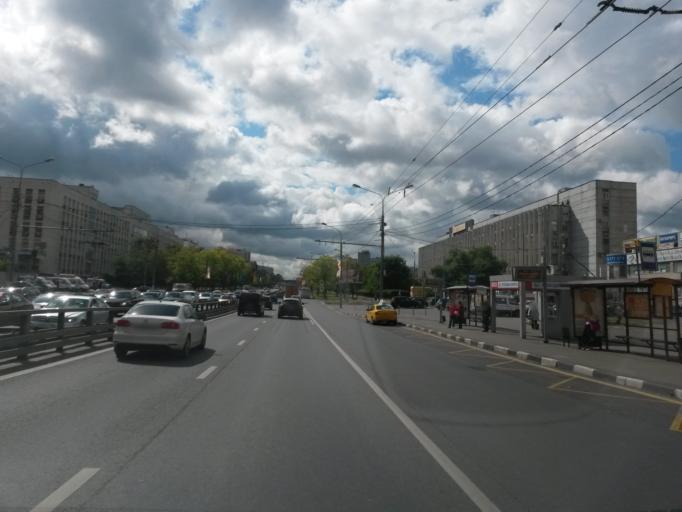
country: RU
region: Moscow
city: Yasenevo
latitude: 55.6417
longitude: 37.5255
